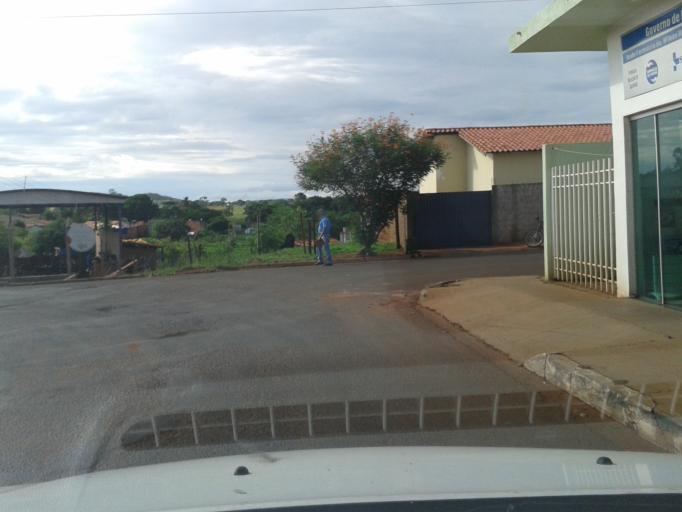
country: BR
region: Minas Gerais
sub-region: Ituiutaba
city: Ituiutaba
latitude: -19.2120
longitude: -49.7855
